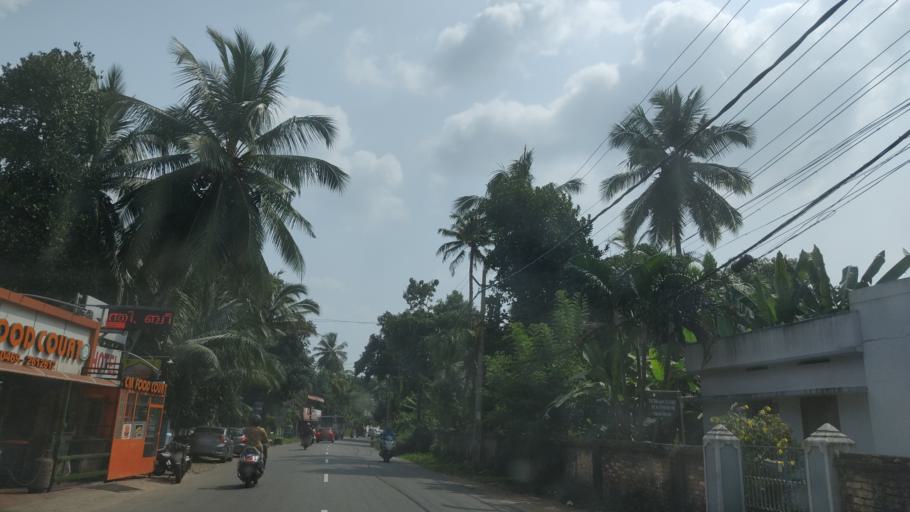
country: IN
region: Kerala
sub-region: Pattanamtitta
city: Tiruvalla
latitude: 9.3365
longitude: 76.5345
